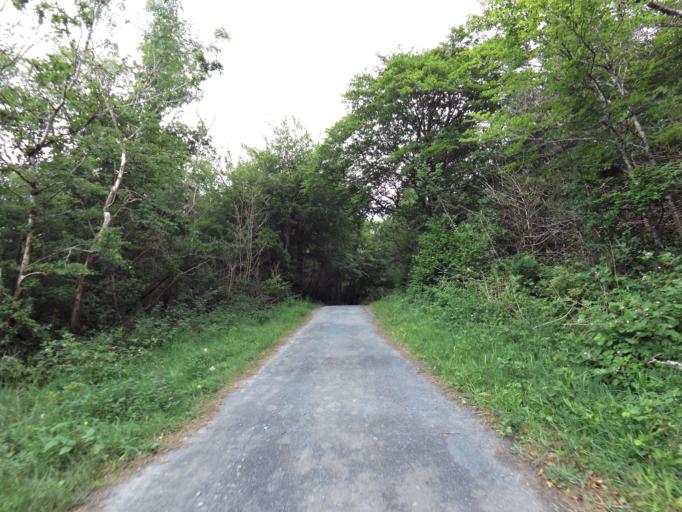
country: IE
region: Connaught
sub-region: County Galway
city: Gort
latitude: 53.0783
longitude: -8.8619
